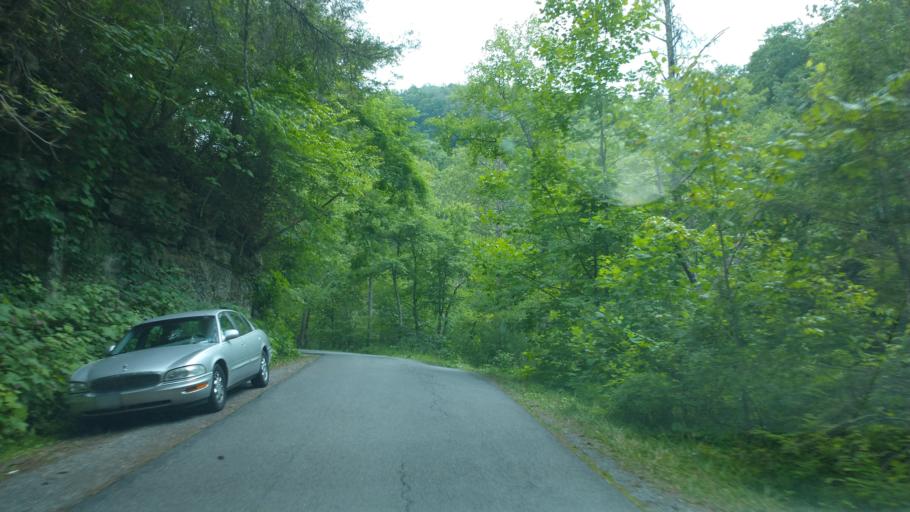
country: US
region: West Virginia
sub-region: Mercer County
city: Athens
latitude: 37.4645
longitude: -81.0643
